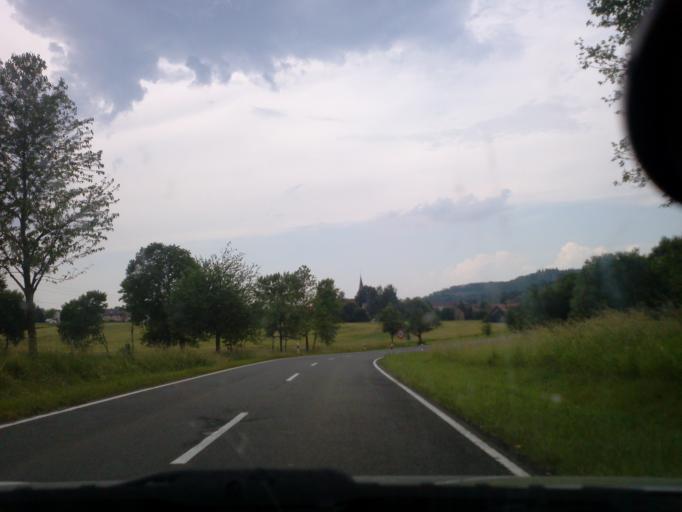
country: DE
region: Baden-Wuerttemberg
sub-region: Karlsruhe Region
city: Sternenfels
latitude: 49.0207
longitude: 8.8541
